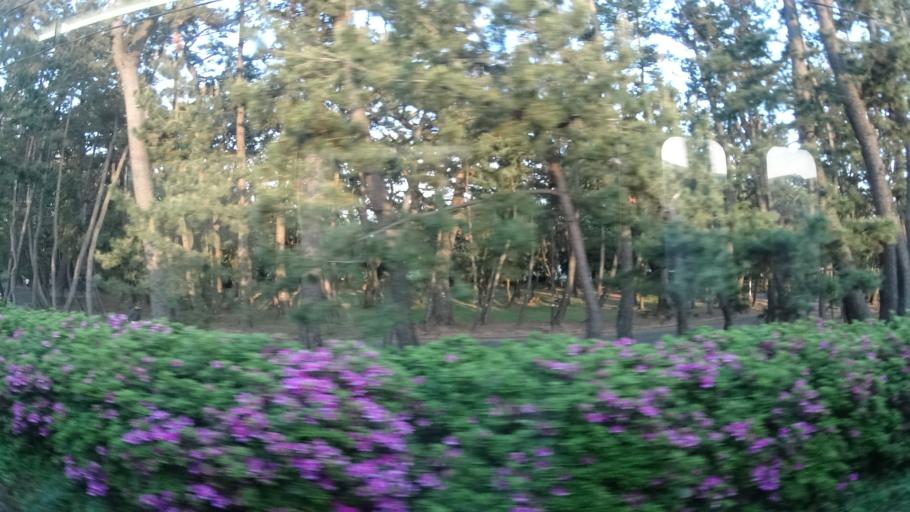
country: JP
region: Aichi
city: Toyohashi
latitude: 34.7277
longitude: 137.3821
